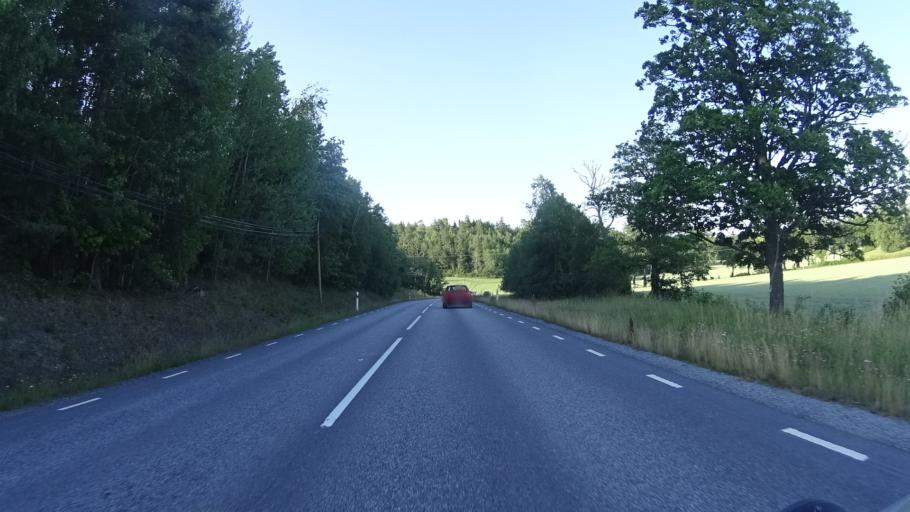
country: SE
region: Stockholm
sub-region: Sodertalje Kommun
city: Pershagen
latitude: 59.0998
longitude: 17.6253
